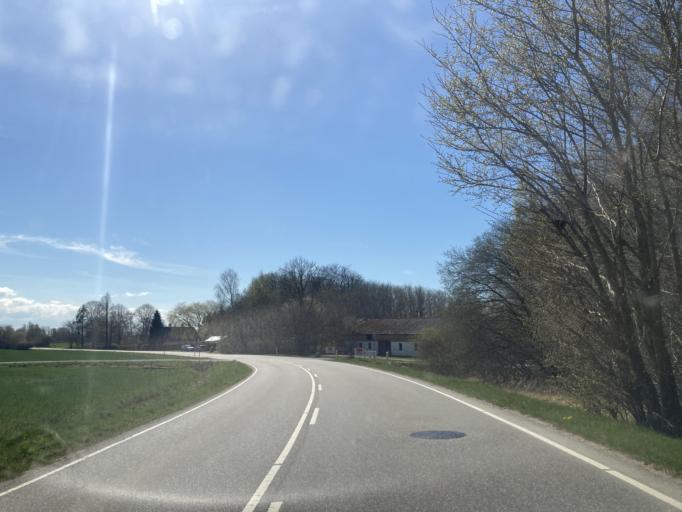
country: DK
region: Capital Region
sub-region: Gribskov Kommune
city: Graested
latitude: 56.0159
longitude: 12.2620
